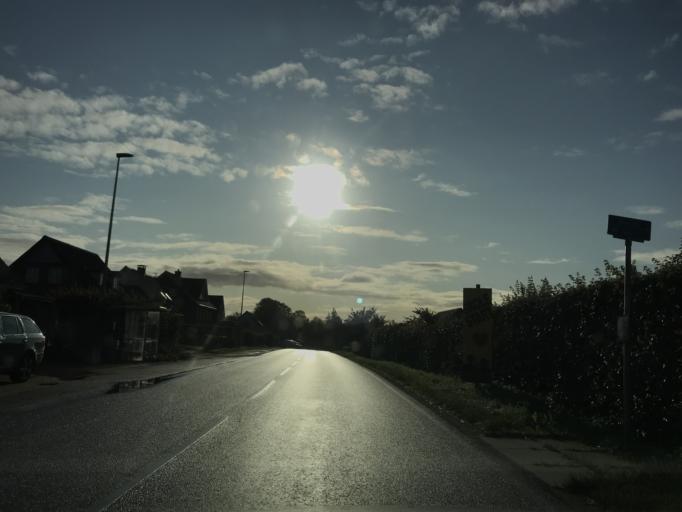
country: DK
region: Central Jutland
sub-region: Skanderborg Kommune
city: Ry
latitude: 56.1779
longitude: 9.7705
